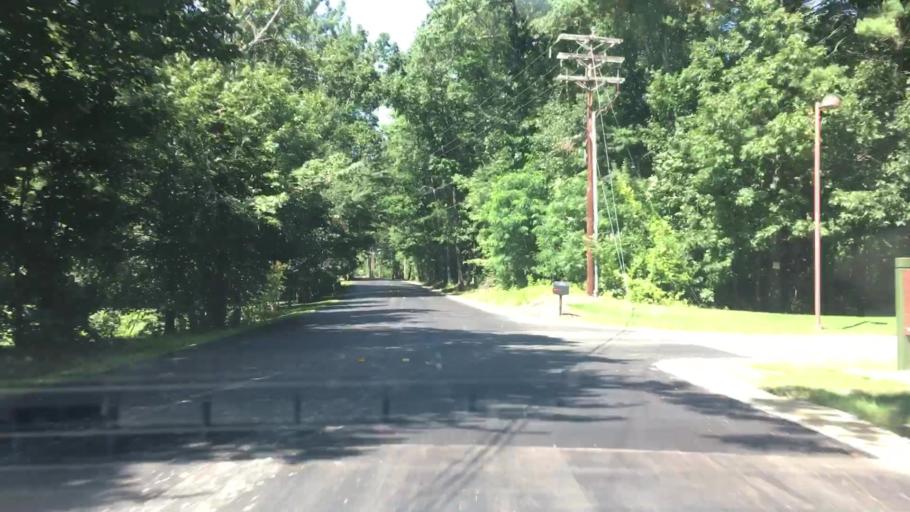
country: US
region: Maine
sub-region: York County
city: Eliot
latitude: 43.1597
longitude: -70.8391
